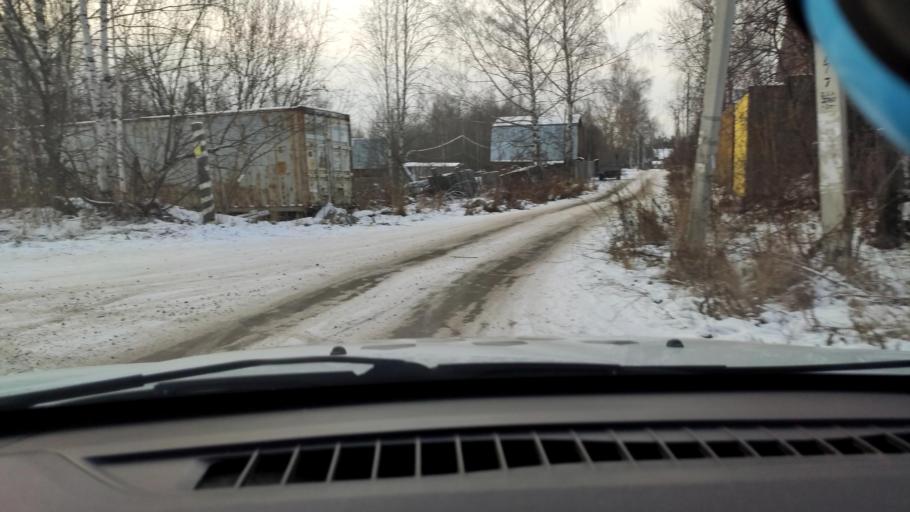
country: RU
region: Perm
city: Kondratovo
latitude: 58.0271
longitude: 56.1686
